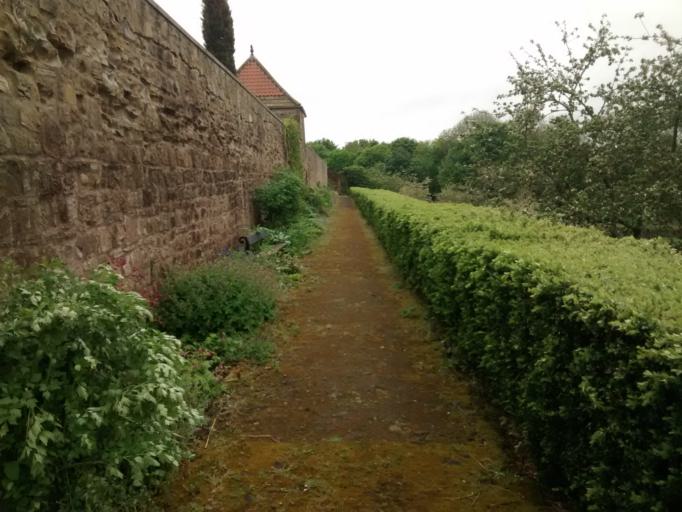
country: GB
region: England
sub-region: County Durham
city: Durham
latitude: 54.7718
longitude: -1.5548
